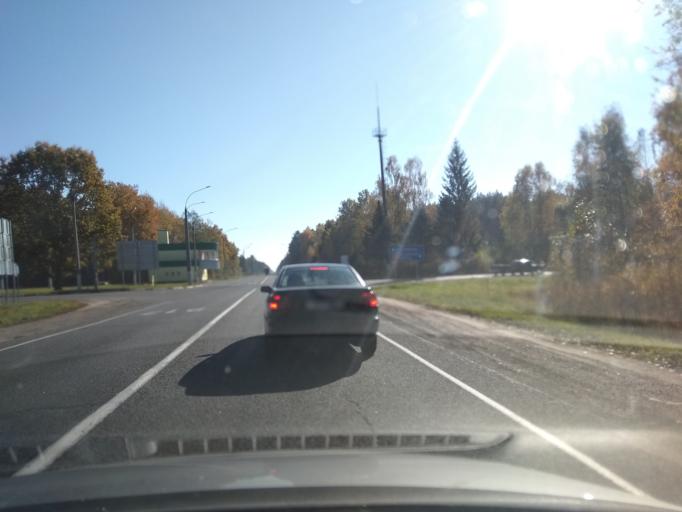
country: BY
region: Brest
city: Malaryta
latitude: 51.8930
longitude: 24.1380
